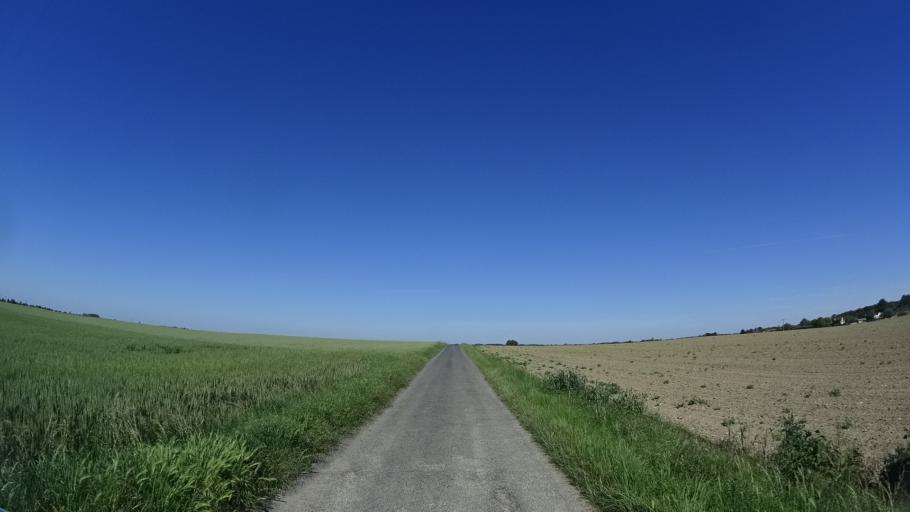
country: FR
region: Pays de la Loire
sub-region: Departement de Maine-et-Loire
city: Doue-la-Fontaine
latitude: 47.2498
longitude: -0.2794
